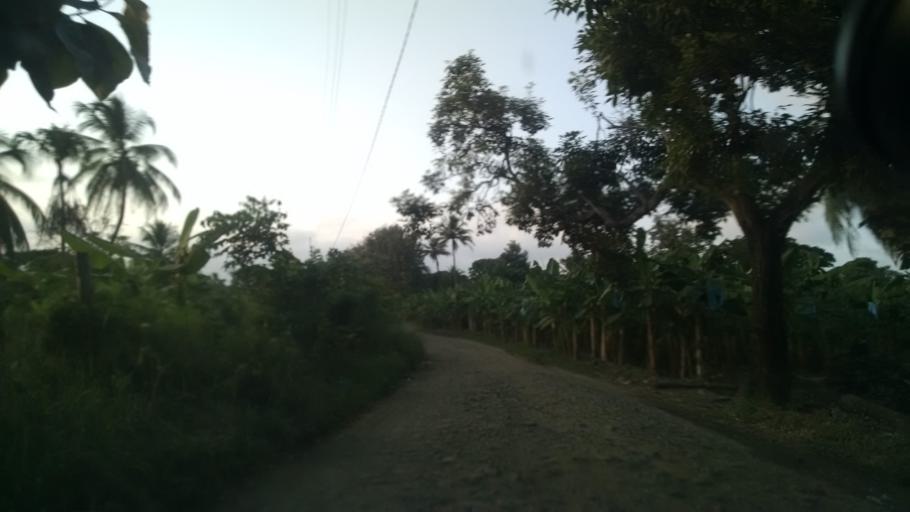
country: CO
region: Antioquia
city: San Juan de Uraba
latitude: 8.7209
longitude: -76.6008
